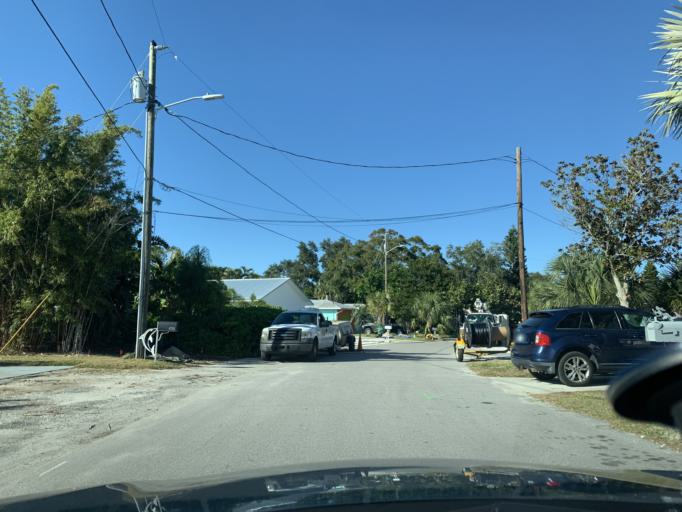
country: US
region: Florida
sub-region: Pinellas County
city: Gulfport
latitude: 27.7379
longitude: -82.6990
